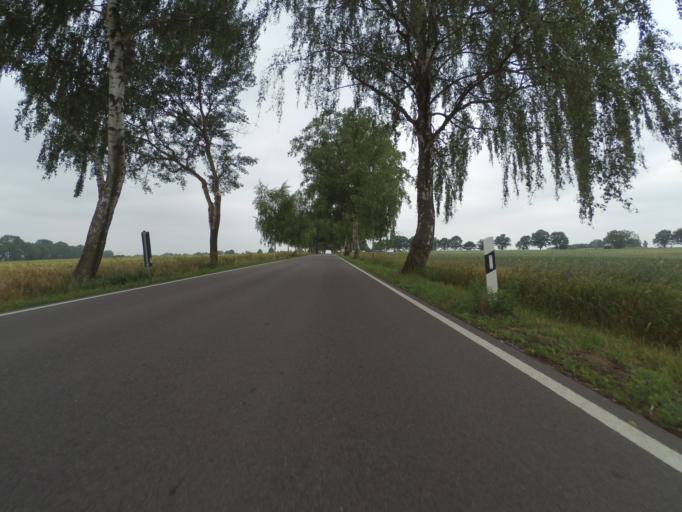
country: DE
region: Mecklenburg-Vorpommern
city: Domsuhl
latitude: 53.4875
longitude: 11.7108
